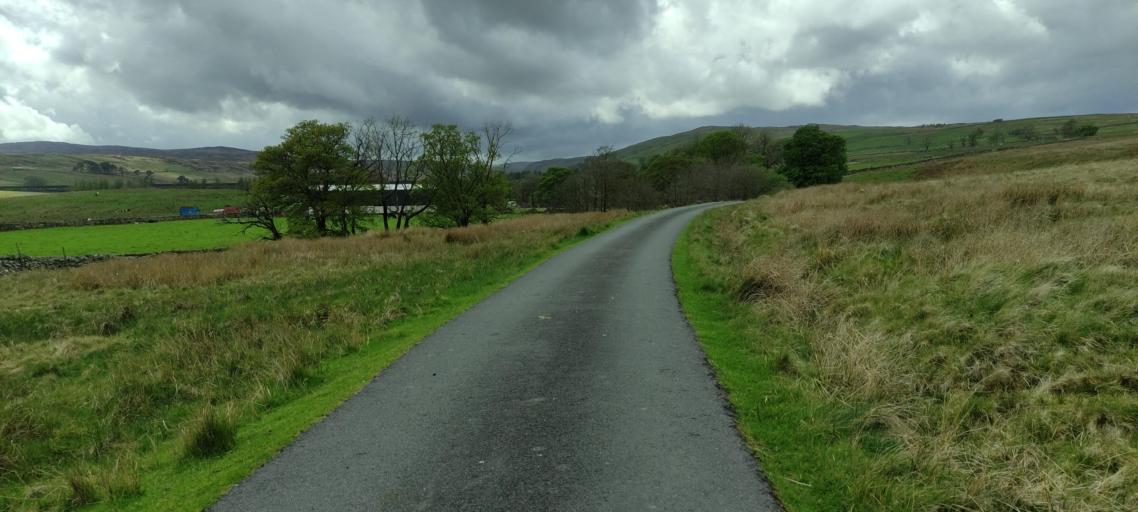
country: GB
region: England
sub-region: Cumbria
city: Penrith
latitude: 54.5038
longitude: -2.6837
